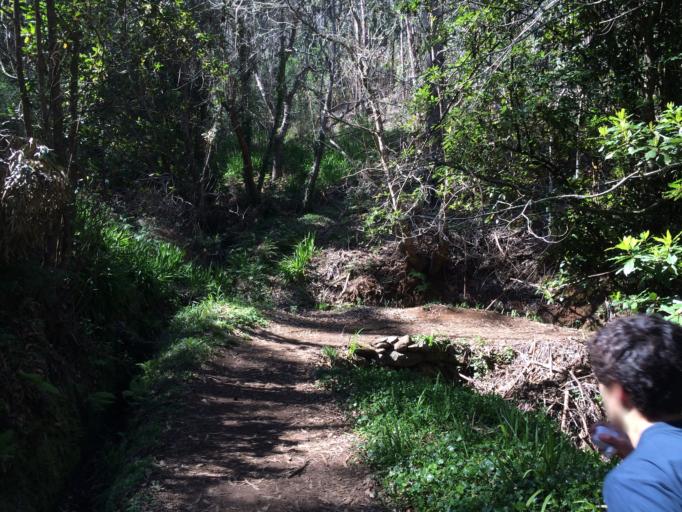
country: PT
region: Madeira
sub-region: Santa Cruz
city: Camacha
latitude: 32.6817
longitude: -16.8576
